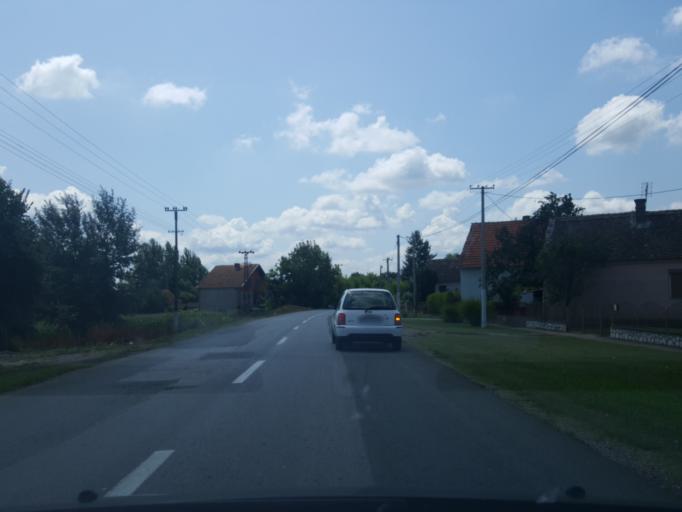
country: RS
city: Salas Nocajski
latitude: 44.9368
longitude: 19.5717
